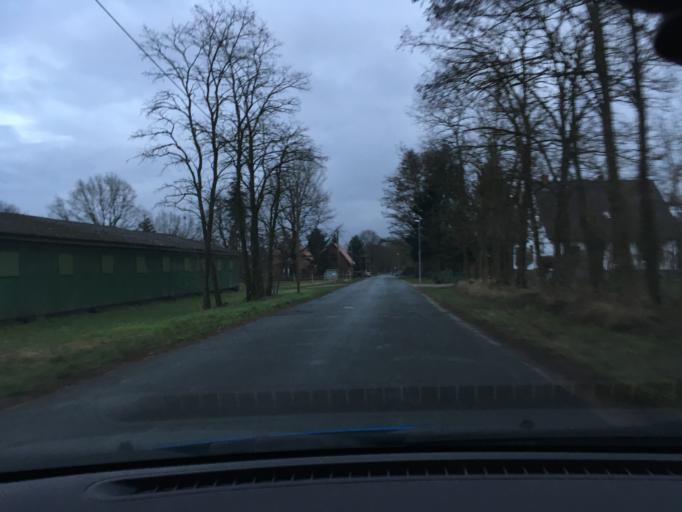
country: DE
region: Mecklenburg-Vorpommern
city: Boizenburg
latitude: 53.3892
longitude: 10.6890
